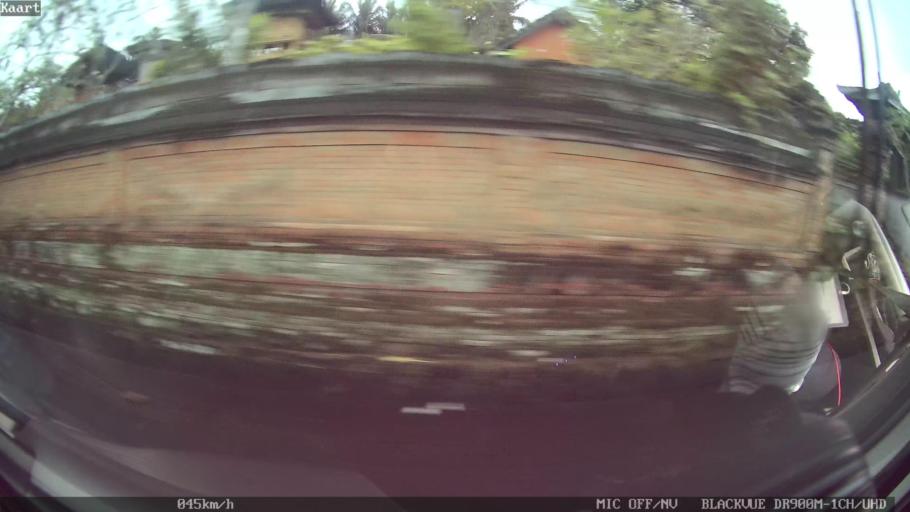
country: ID
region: Bali
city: Banjar Teguan
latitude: -8.5195
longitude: 115.2287
